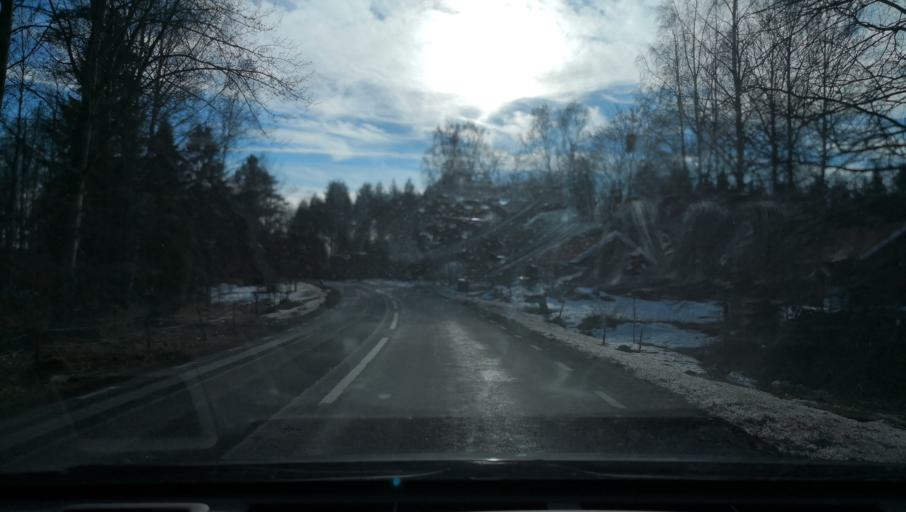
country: SE
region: Uppsala
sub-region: Osthammars Kommun
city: Osterbybruk
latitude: 60.2767
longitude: 17.9614
